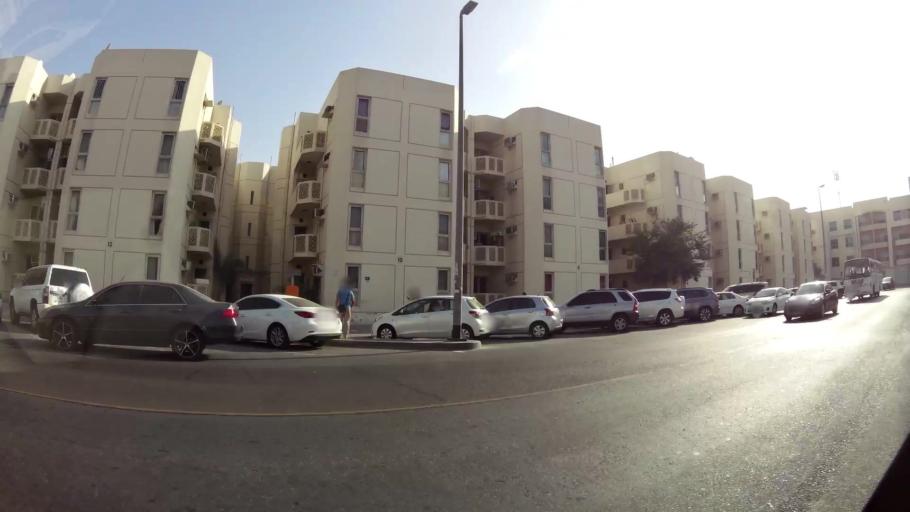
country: AE
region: Ash Shariqah
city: Sharjah
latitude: 25.2406
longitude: 55.2996
